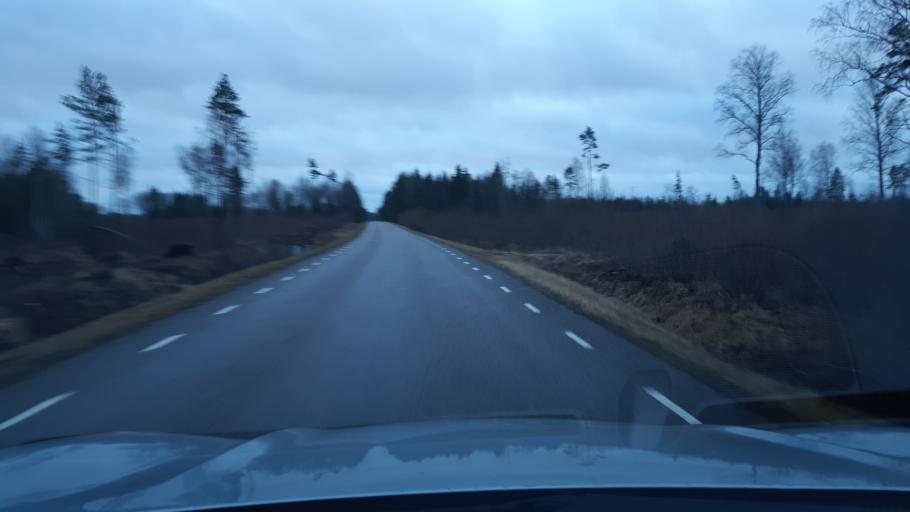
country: EE
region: Raplamaa
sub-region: Kohila vald
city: Kohila
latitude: 59.0839
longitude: 24.6754
